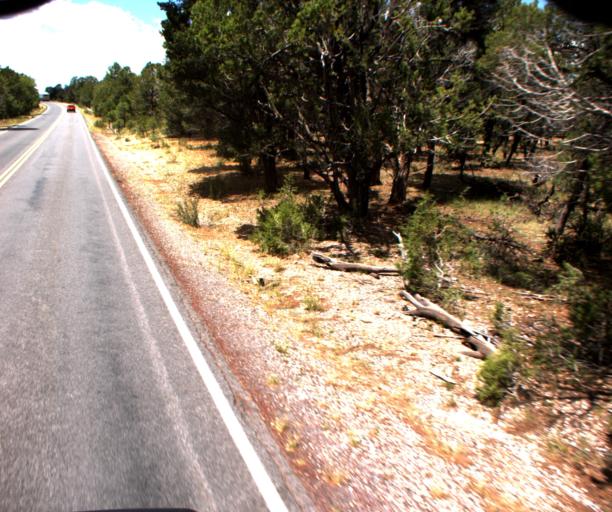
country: US
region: Arizona
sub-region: Coconino County
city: Grand Canyon
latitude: 36.0072
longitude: -112.0493
